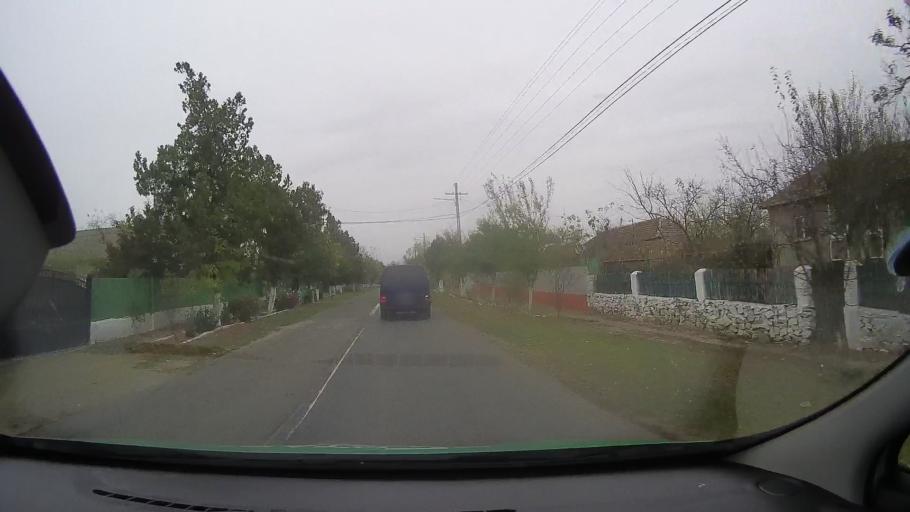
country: RO
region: Constanta
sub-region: Comuna Vulturu
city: Vulturu
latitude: 44.7027
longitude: 28.2344
